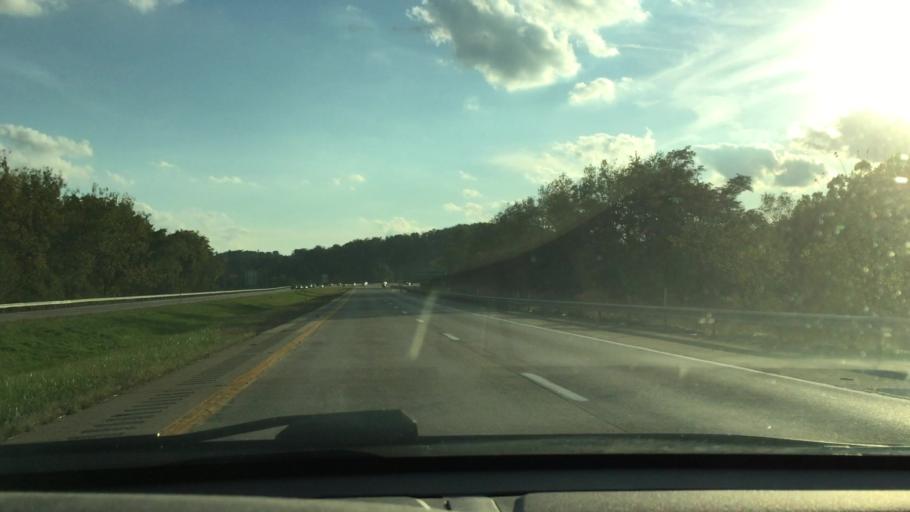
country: US
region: Pennsylvania
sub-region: Washington County
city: McGovern
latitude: 40.2155
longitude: -80.2192
